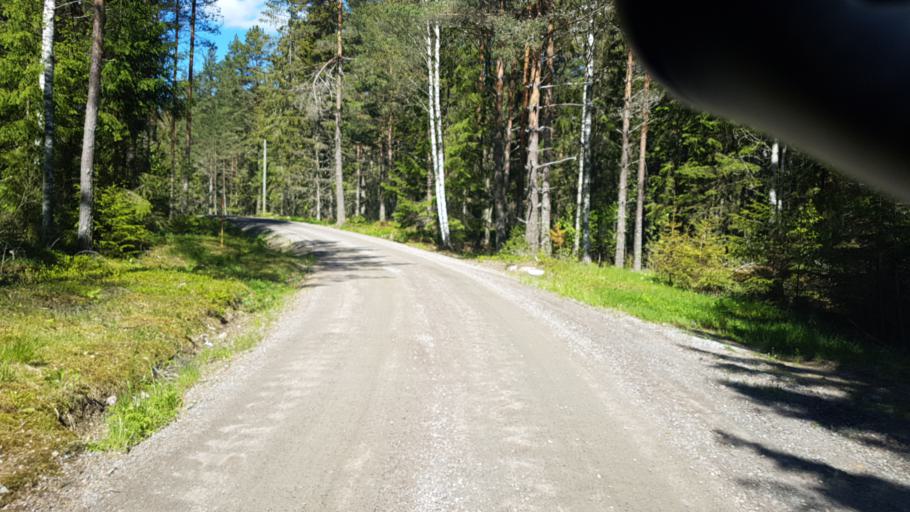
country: SE
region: Vaermland
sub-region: Arvika Kommun
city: Arvika
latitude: 59.5600
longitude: 12.8432
